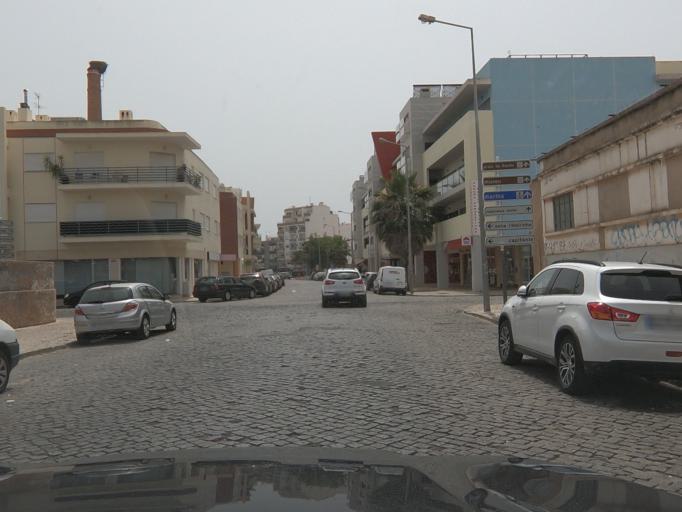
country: PT
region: Faro
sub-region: Portimao
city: Portimao
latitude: 37.1333
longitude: -8.5363
